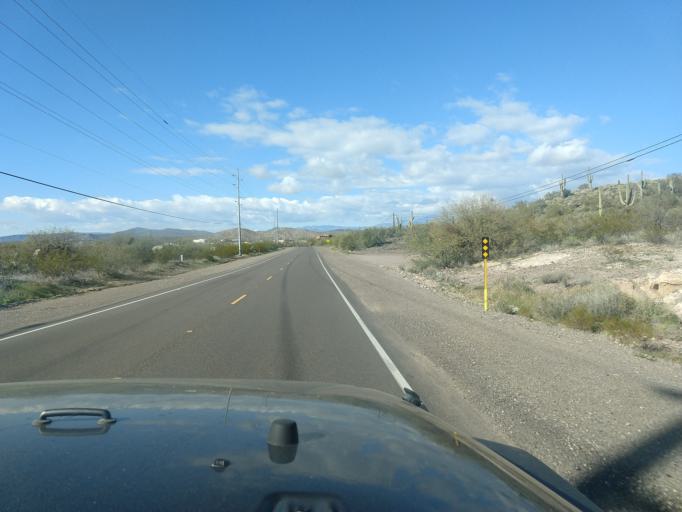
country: US
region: Arizona
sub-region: Maricopa County
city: New River
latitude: 33.9202
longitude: -112.1050
